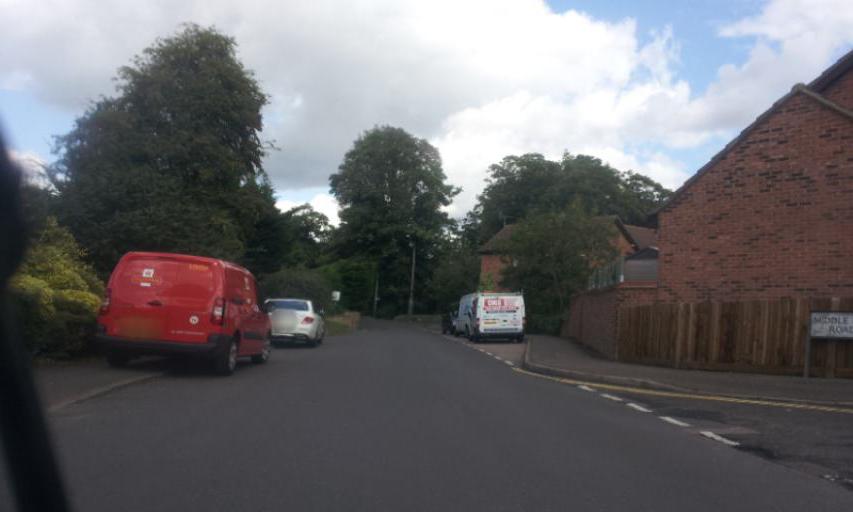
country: GB
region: England
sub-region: Kent
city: Larkfield
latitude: 51.2902
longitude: 0.4303
